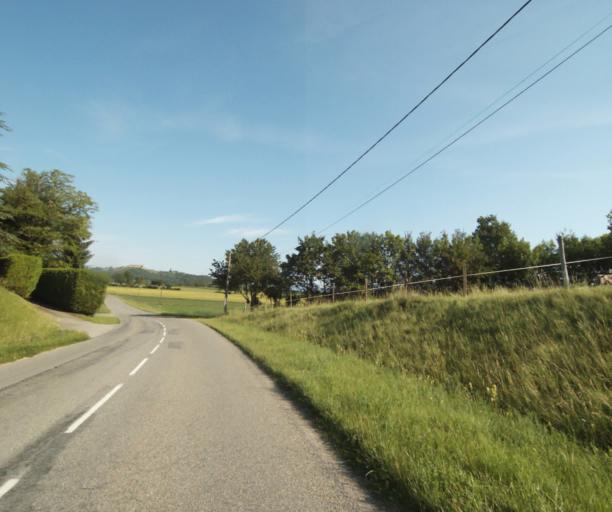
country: FR
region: Rhone-Alpes
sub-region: Departement de la Haute-Savoie
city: Allinges
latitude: 46.3161
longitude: 6.4833
